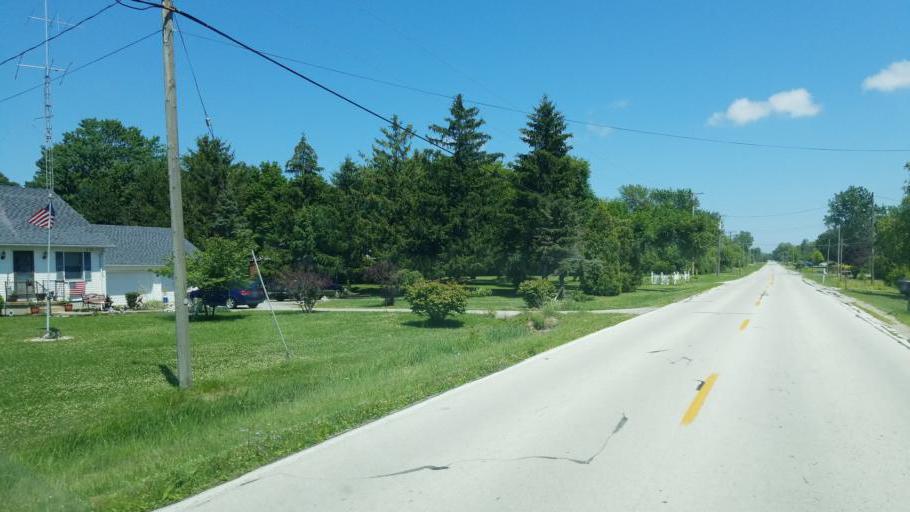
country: US
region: Ohio
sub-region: Ottawa County
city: Port Clinton
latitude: 41.4940
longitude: -82.9157
